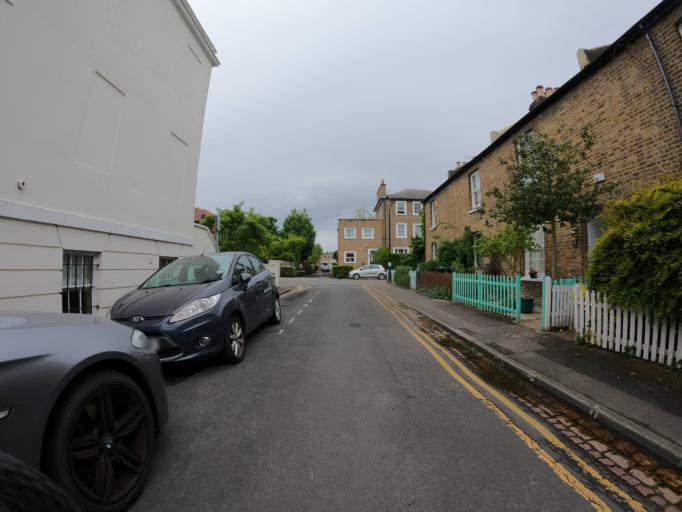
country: GB
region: England
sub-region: Greater London
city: Ealing
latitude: 51.5081
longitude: -0.3022
